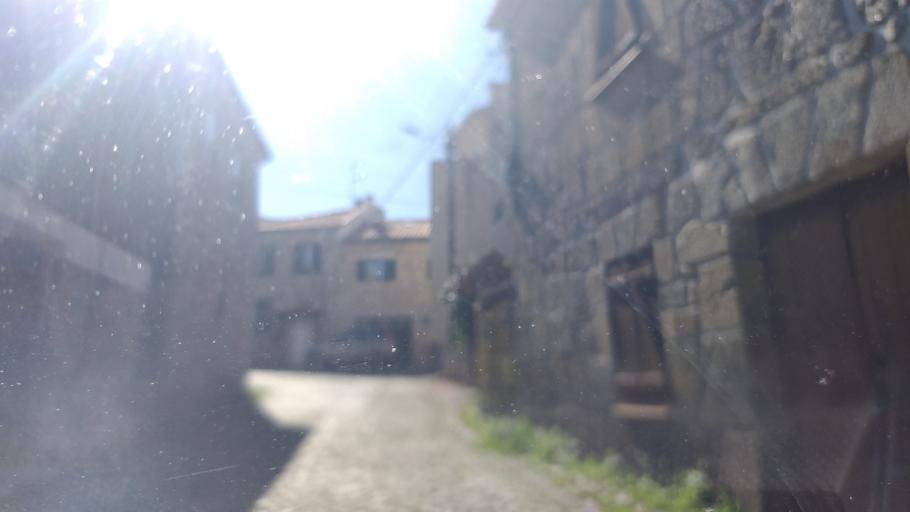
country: PT
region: Guarda
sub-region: Manteigas
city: Manteigas
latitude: 40.4694
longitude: -7.5992
